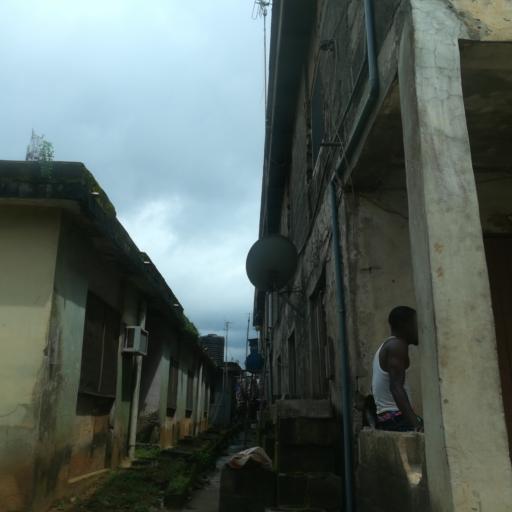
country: NG
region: Lagos
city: Agege
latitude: 6.6024
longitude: 3.2938
